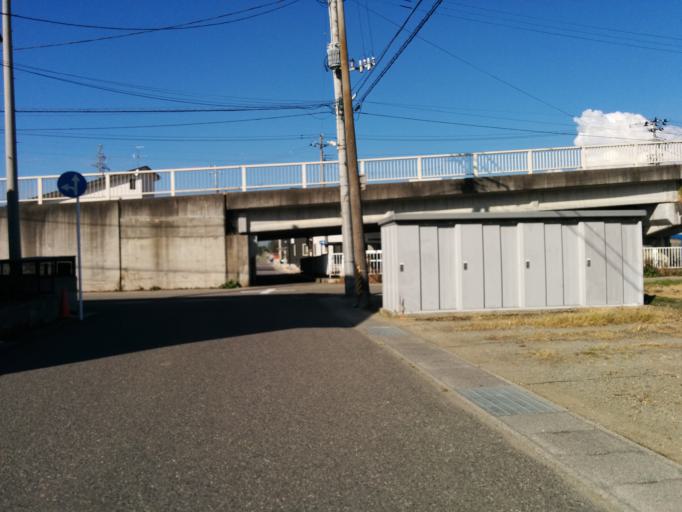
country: JP
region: Fukushima
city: Kitakata
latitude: 37.4786
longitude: 139.9125
